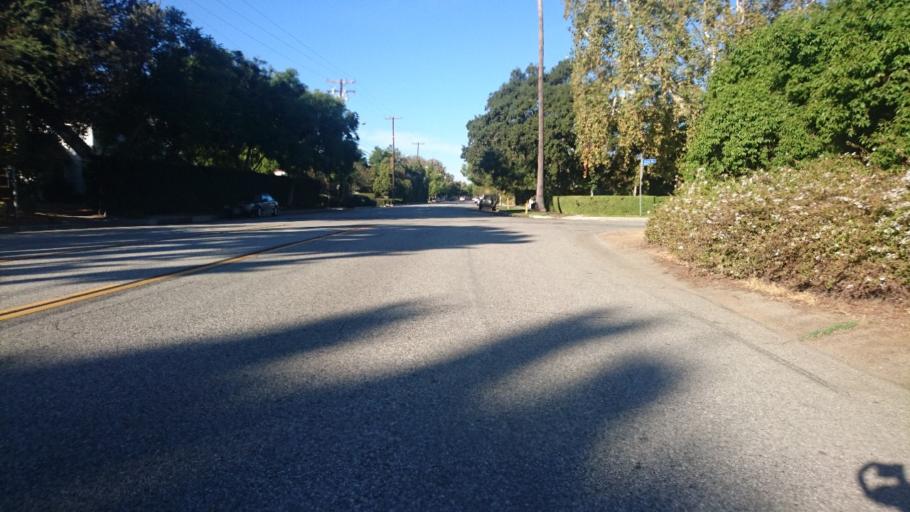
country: US
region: California
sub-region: Los Angeles County
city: East Pasadena
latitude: 34.1379
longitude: -118.1058
